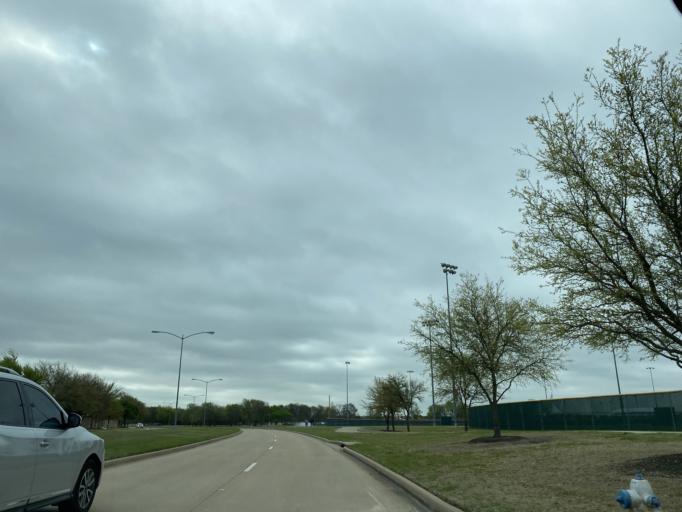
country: US
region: Texas
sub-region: Collin County
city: Allen
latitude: 33.1108
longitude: -96.6269
